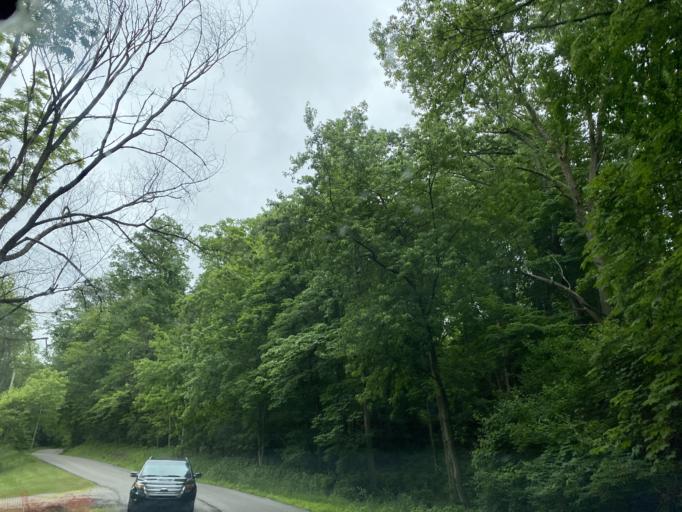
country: US
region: Kentucky
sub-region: Campbell County
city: Dayton
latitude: 39.1019
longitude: -84.4612
